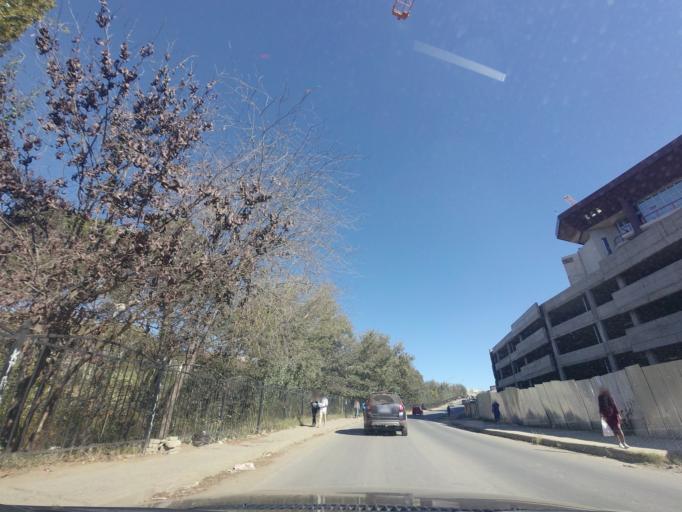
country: LS
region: Maseru
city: Maseru
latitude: -29.3132
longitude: 27.4898
